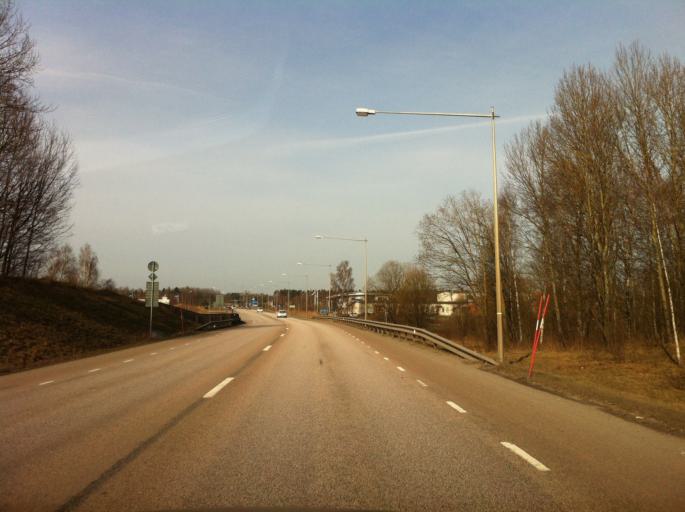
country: SE
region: Vaestra Goetaland
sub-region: Skovde Kommun
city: Skoevde
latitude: 58.3905
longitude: 13.8748
